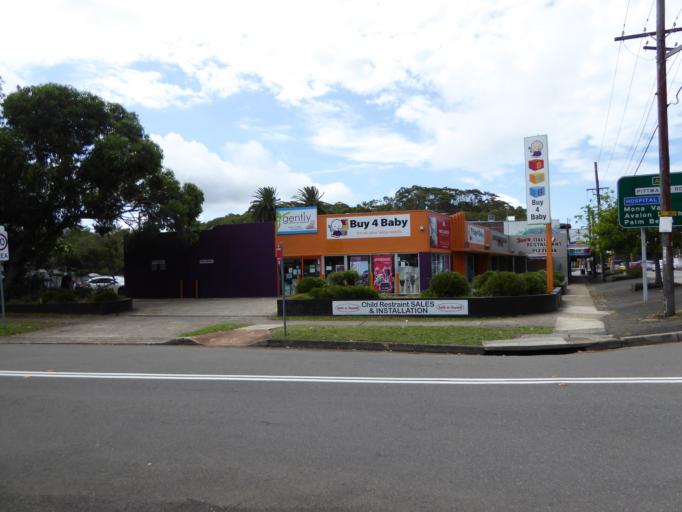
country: AU
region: New South Wales
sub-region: Pittwater
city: North Narrabeen
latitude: -33.7087
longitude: 151.2960
